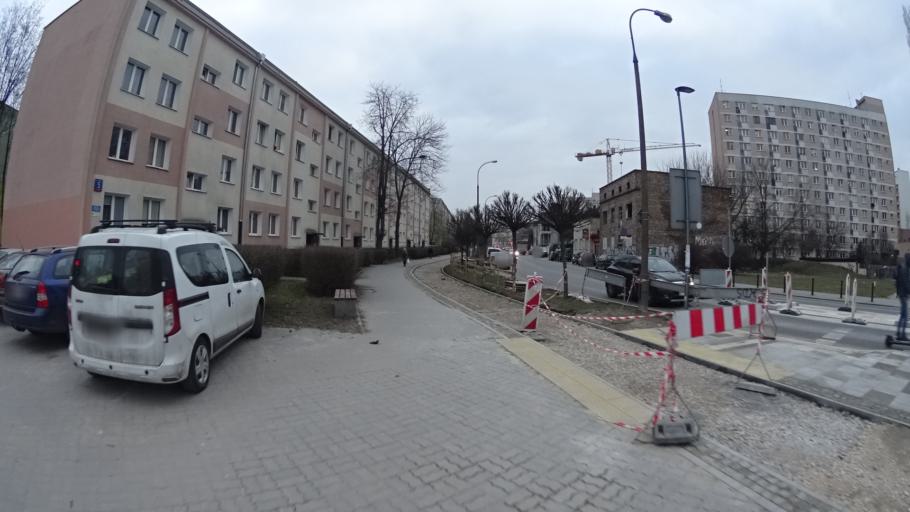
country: PL
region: Masovian Voivodeship
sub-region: Warszawa
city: Bemowo
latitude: 52.2377
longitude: 20.9431
